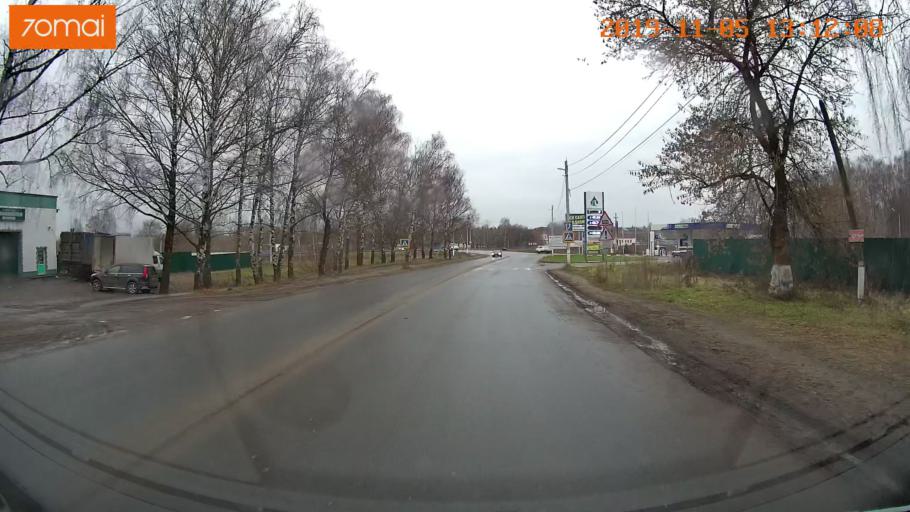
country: RU
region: Ivanovo
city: Shuya
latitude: 56.8574
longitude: 41.3491
